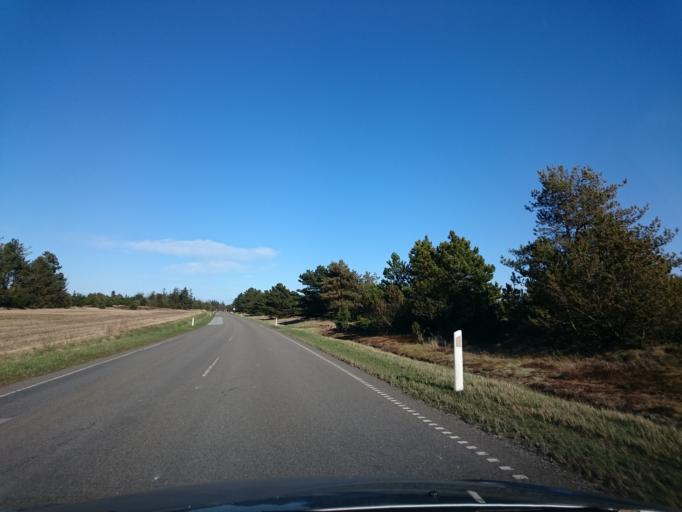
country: DK
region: North Denmark
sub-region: Frederikshavn Kommune
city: Strandby
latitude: 57.6055
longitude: 10.3794
